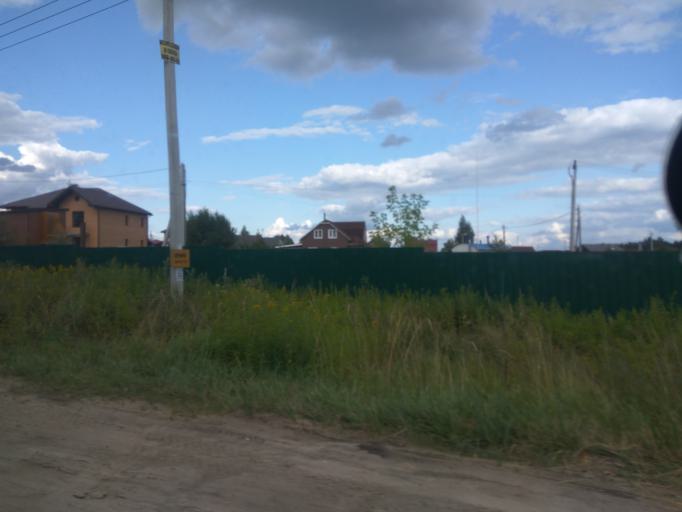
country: RU
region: Moskovskaya
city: Bronnitsy
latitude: 55.4558
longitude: 38.2729
